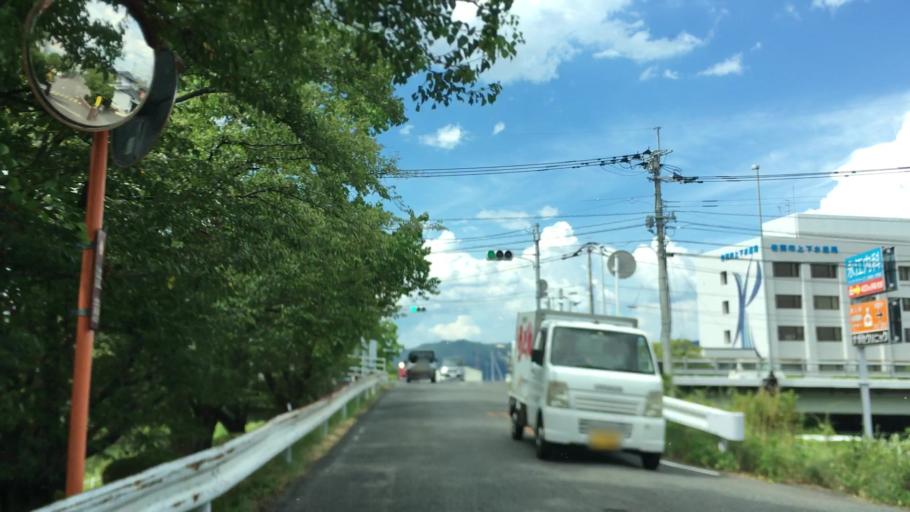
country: JP
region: Saga Prefecture
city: Saga-shi
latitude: 33.2725
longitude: 130.2823
